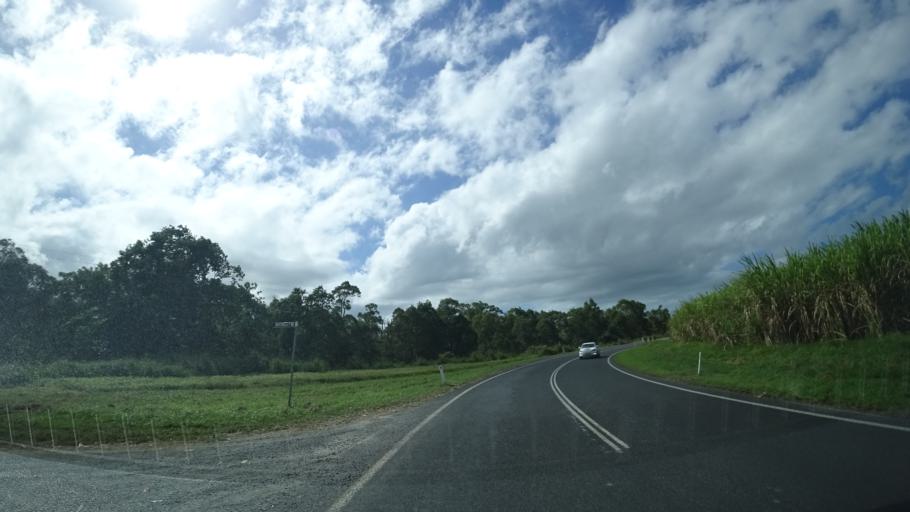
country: AU
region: Queensland
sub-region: Cairns
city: Port Douglas
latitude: -16.2793
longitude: 145.3800
